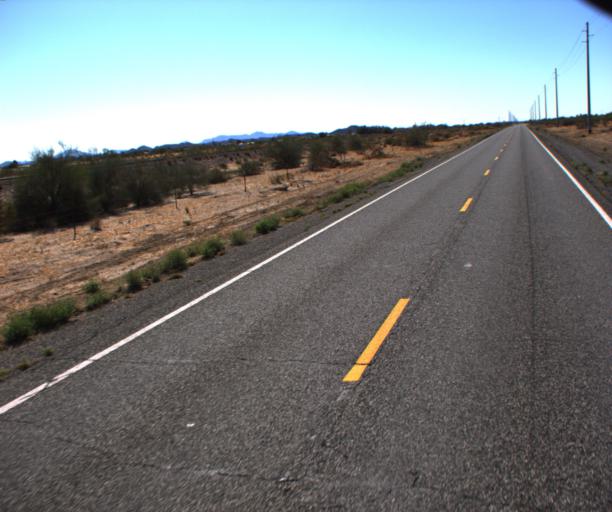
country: US
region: Arizona
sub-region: La Paz County
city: Cienega Springs
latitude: 33.9668
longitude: -114.0381
